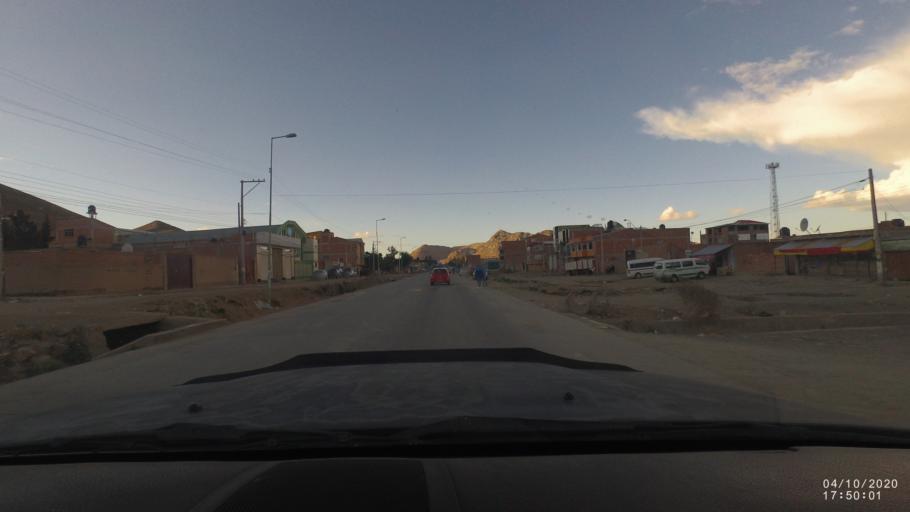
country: BO
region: Oruro
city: Oruro
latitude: -18.0044
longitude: -67.1359
